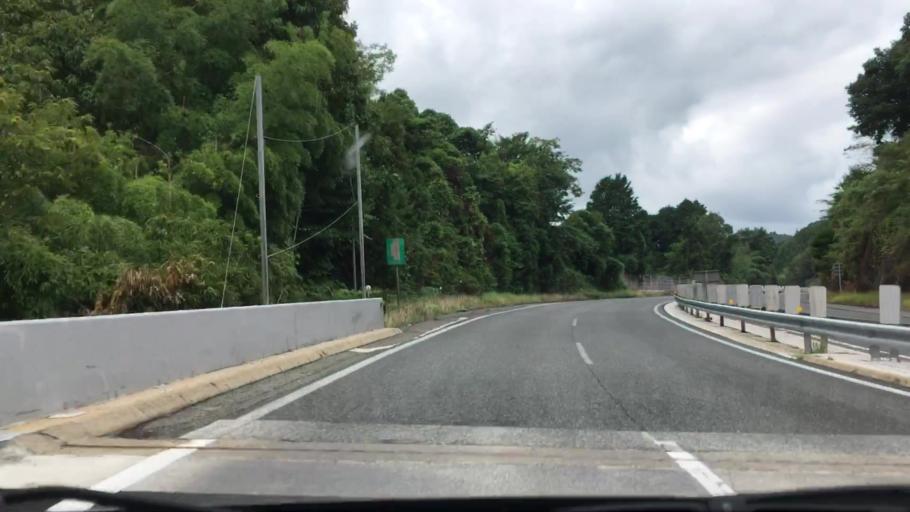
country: JP
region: Okayama
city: Niimi
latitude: 35.0087
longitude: 133.5096
